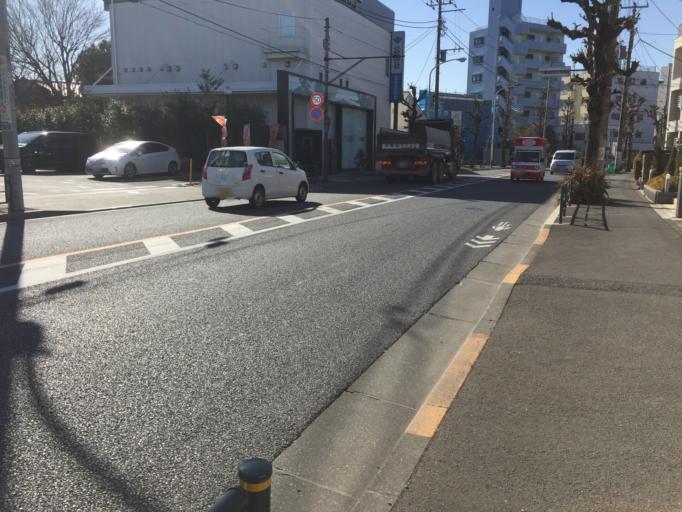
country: JP
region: Tokyo
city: Chofugaoka
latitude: 35.6341
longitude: 139.5916
